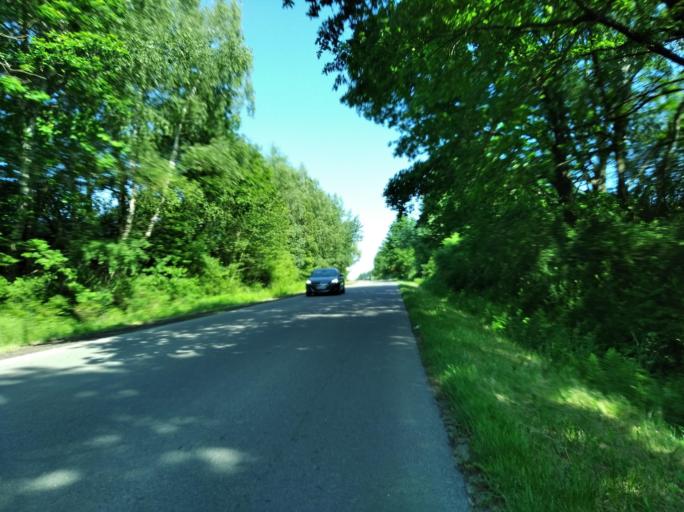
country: PL
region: Subcarpathian Voivodeship
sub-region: Powiat ropczycko-sedziszowski
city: Wielopole Skrzynskie
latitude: 49.9531
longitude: 21.6185
